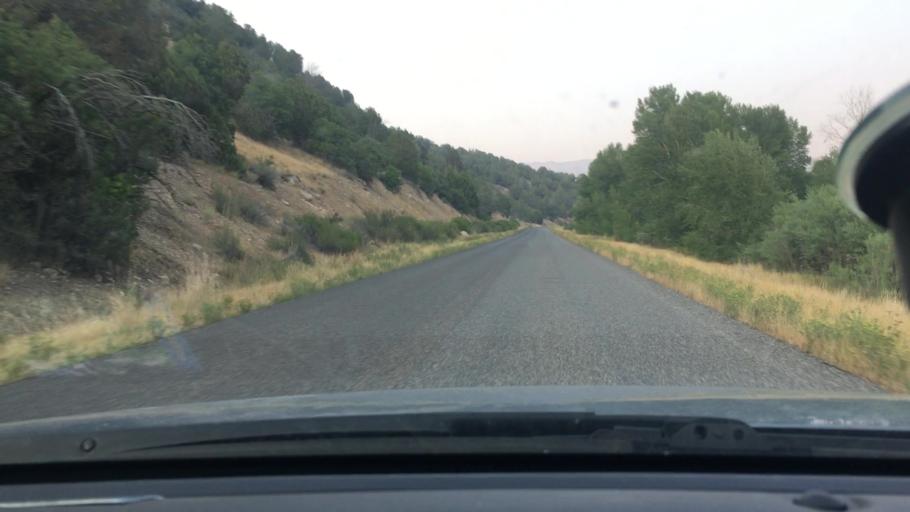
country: US
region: Utah
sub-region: Utah County
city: Mapleton
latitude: 40.0546
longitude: -111.4611
